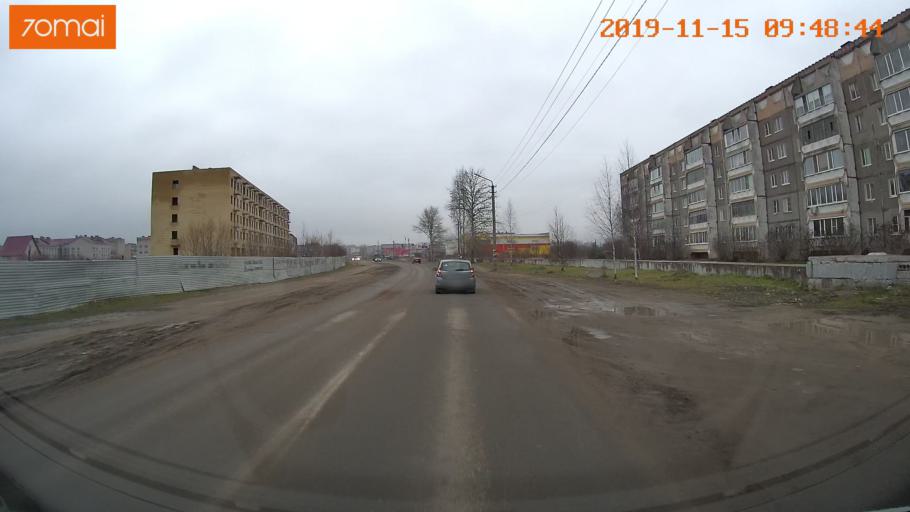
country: RU
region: Vologda
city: Sheksna
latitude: 59.2248
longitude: 38.5135
